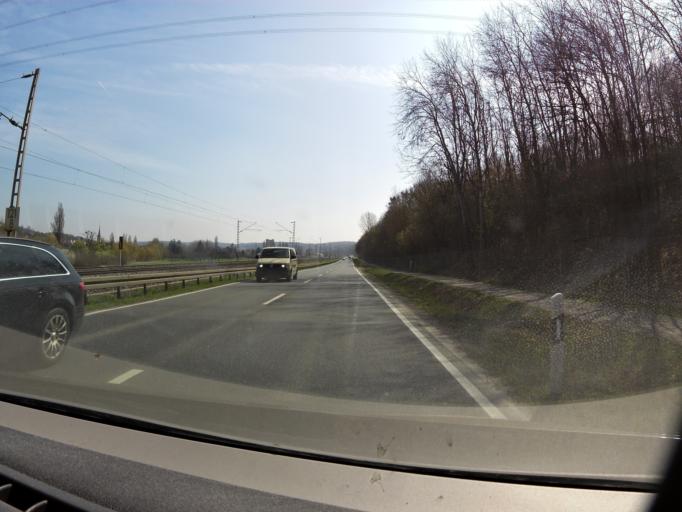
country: DE
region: Bavaria
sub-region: Regierungsbezirk Unterfranken
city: Ochsenfurt
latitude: 49.6746
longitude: 10.0381
